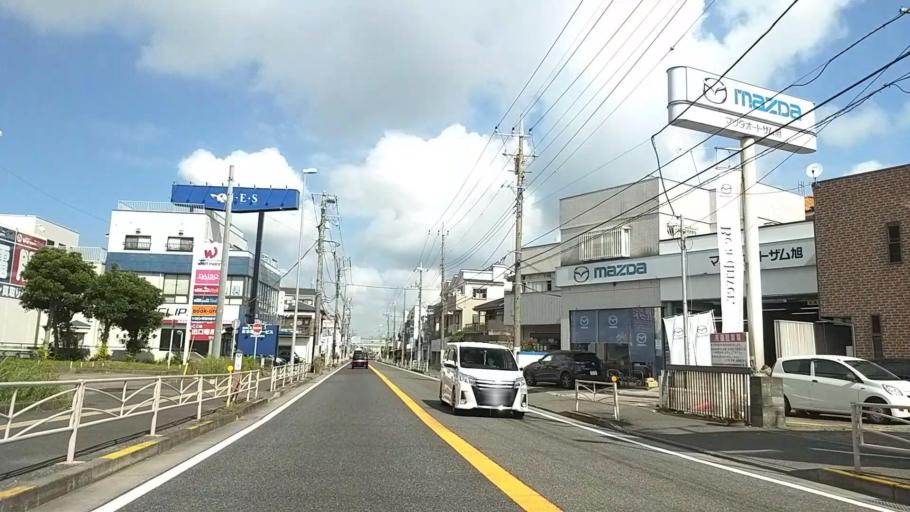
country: JP
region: Kanagawa
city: Minami-rinkan
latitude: 35.4780
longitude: 139.5398
